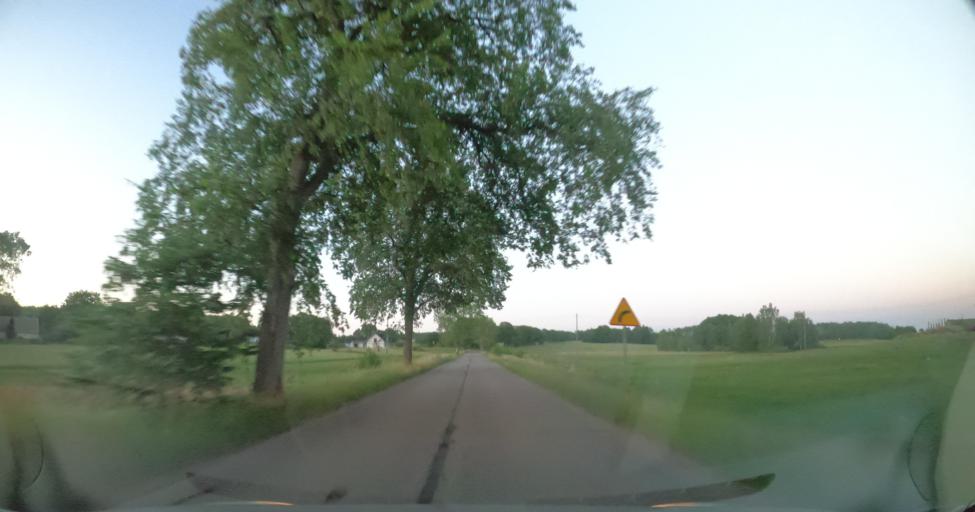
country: PL
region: Pomeranian Voivodeship
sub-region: Powiat wejherowski
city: Szemud
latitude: 54.4689
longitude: 18.1497
